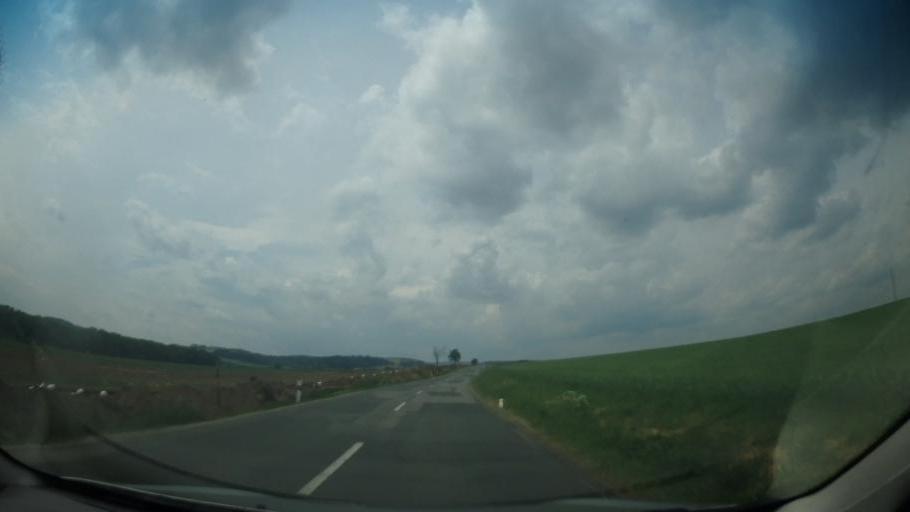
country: CZ
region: South Moravian
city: Boritov
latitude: 49.4333
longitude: 16.5720
